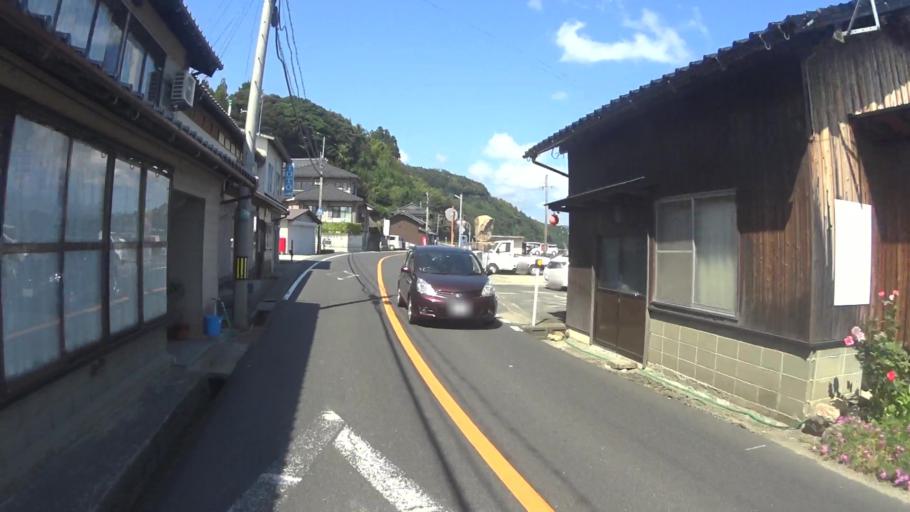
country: JP
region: Kyoto
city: Miyazu
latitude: 35.6262
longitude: 135.2456
